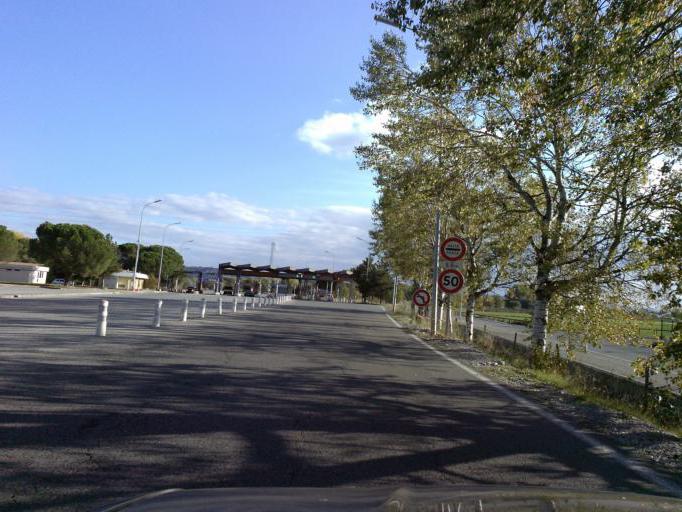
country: FR
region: Provence-Alpes-Cote d'Azur
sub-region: Departement des Alpes-de-Haute-Provence
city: Manosque
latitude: 43.8091
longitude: 5.8121
